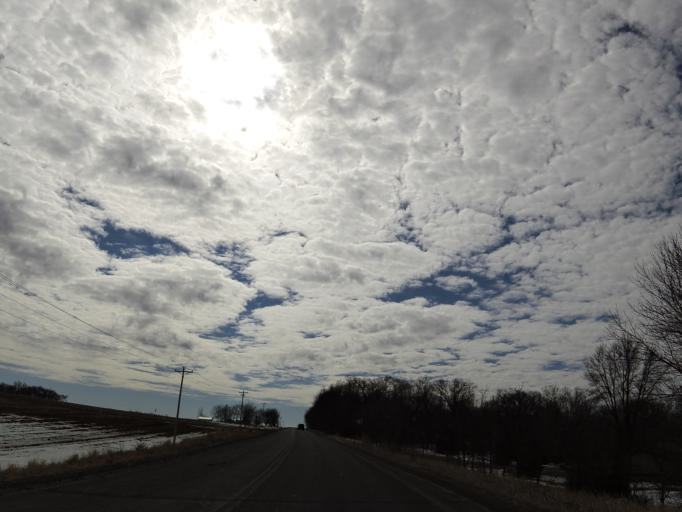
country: US
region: Minnesota
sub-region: Le Sueur County
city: New Prague
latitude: 44.6027
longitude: -93.5577
